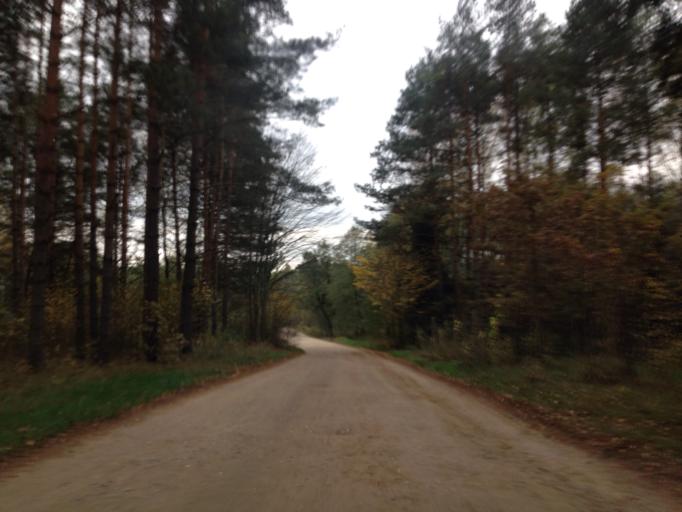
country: PL
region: Kujawsko-Pomorskie
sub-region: Powiat brodnicki
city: Bartniczka
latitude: 53.2817
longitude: 19.5821
